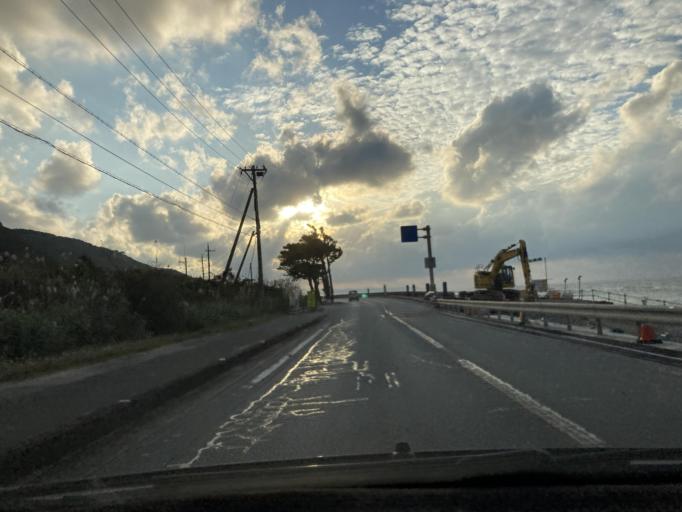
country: JP
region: Okinawa
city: Nago
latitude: 26.7822
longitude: 128.2155
